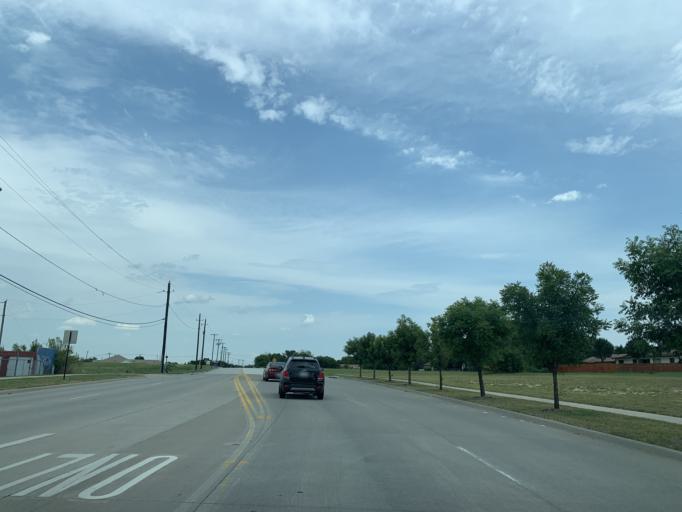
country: US
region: Texas
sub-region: Tarrant County
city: Watauga
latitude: 32.8372
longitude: -97.2762
